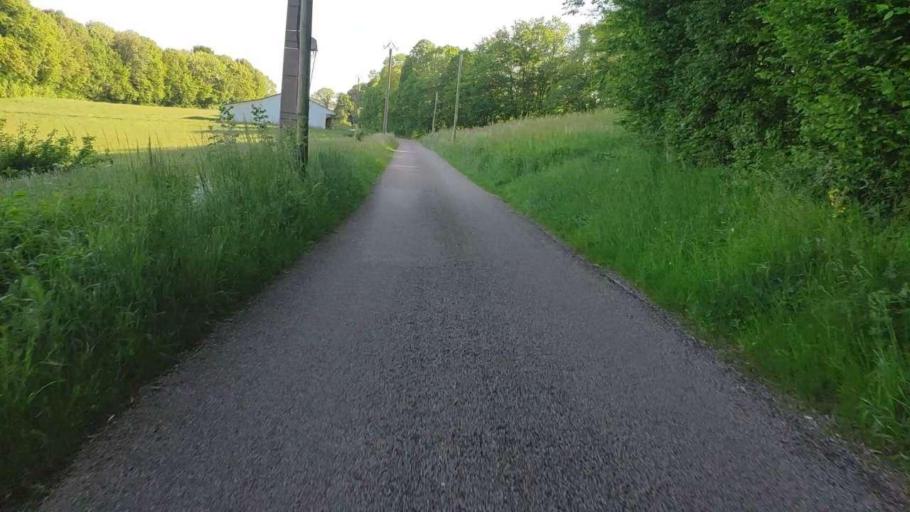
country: FR
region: Franche-Comte
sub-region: Departement du Jura
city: Perrigny
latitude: 46.7125
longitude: 5.6208
